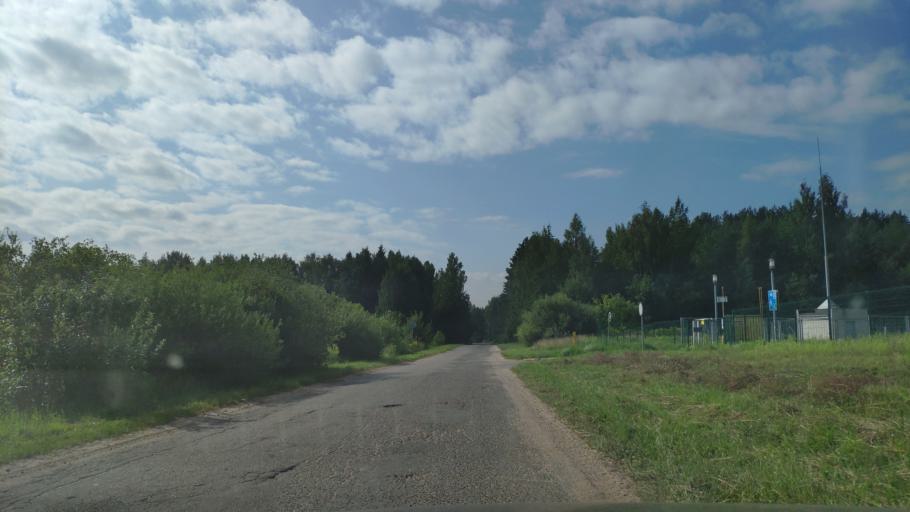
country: BY
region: Minsk
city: Zaslawye
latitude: 53.9842
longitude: 27.2891
